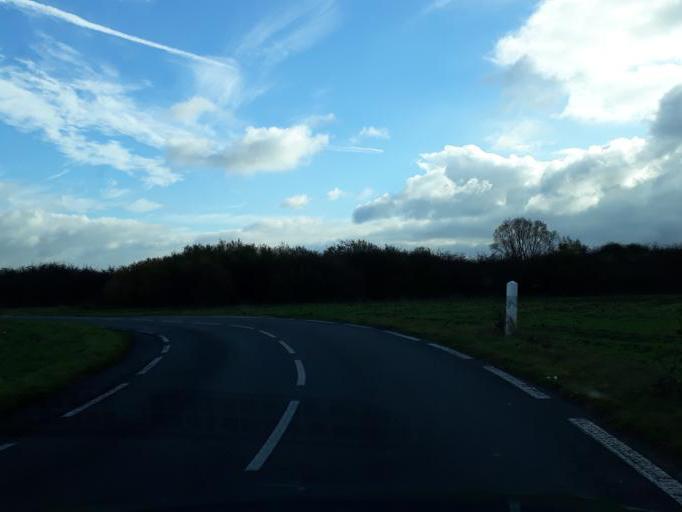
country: FR
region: Centre
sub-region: Departement du Loiret
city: Saint-Jean-de-la-Ruelle
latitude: 47.9284
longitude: 1.8708
